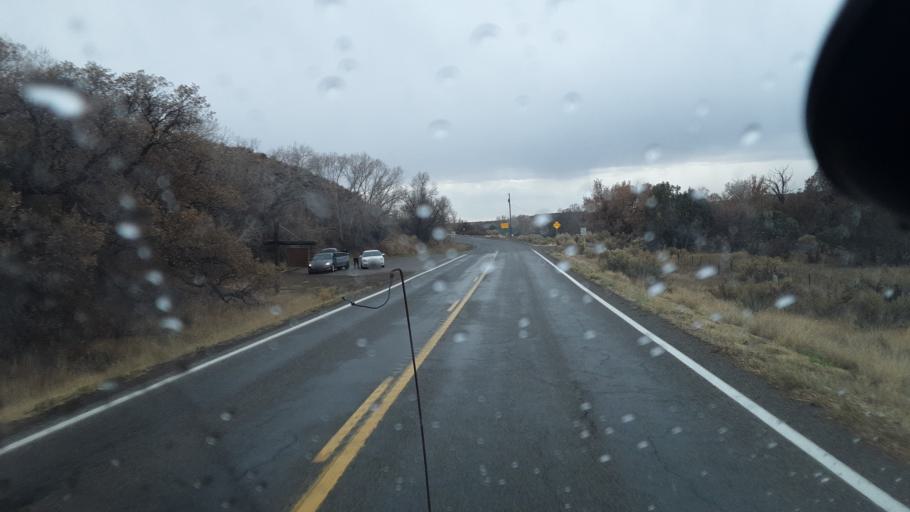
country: US
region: New Mexico
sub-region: San Juan County
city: Spencerville
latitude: 37.0011
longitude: -108.1860
